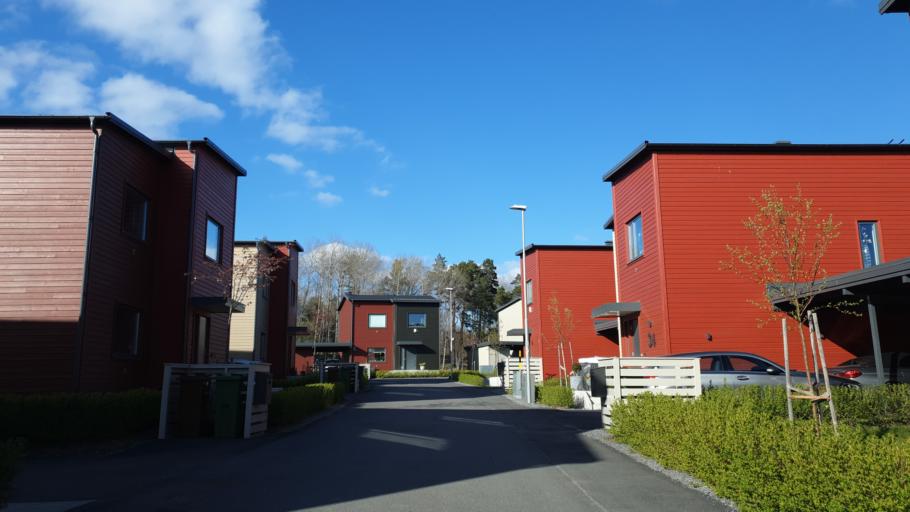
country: SE
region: Stockholm
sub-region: Upplands Vasby Kommun
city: Upplands Vaesby
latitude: 59.5157
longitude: 17.8771
